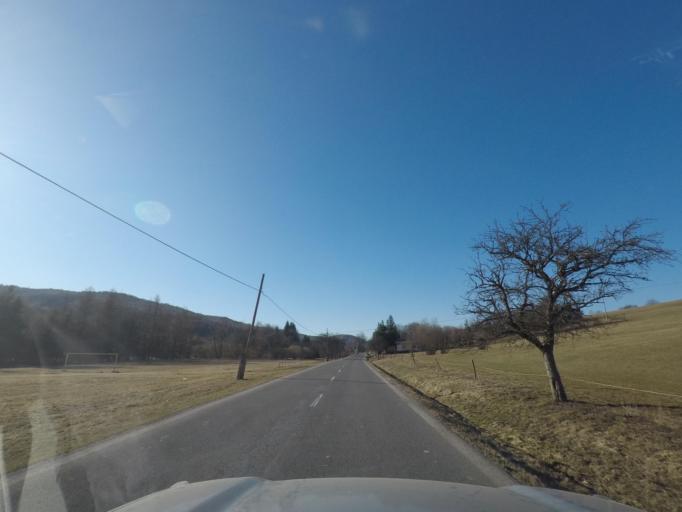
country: SK
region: Presovsky
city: Medzilaborce
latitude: 49.1883
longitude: 22.0097
